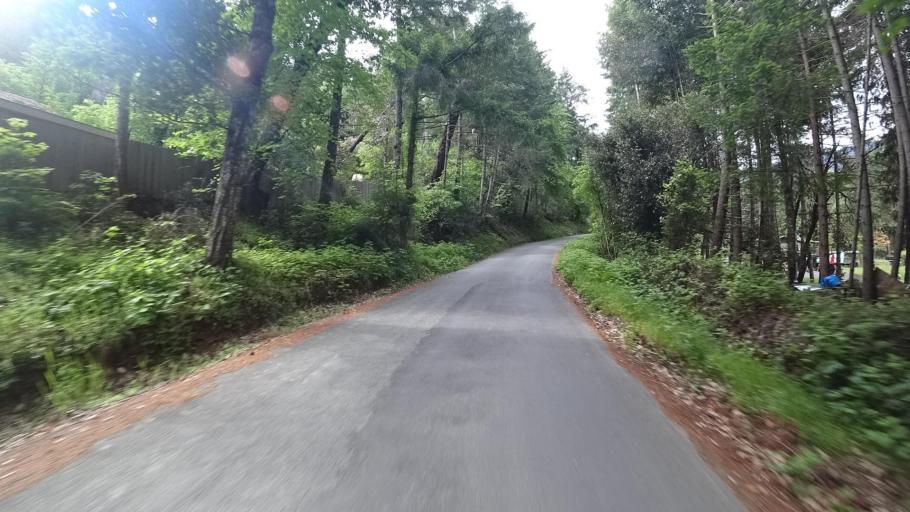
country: US
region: California
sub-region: Humboldt County
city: Willow Creek
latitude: 40.9379
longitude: -123.6152
